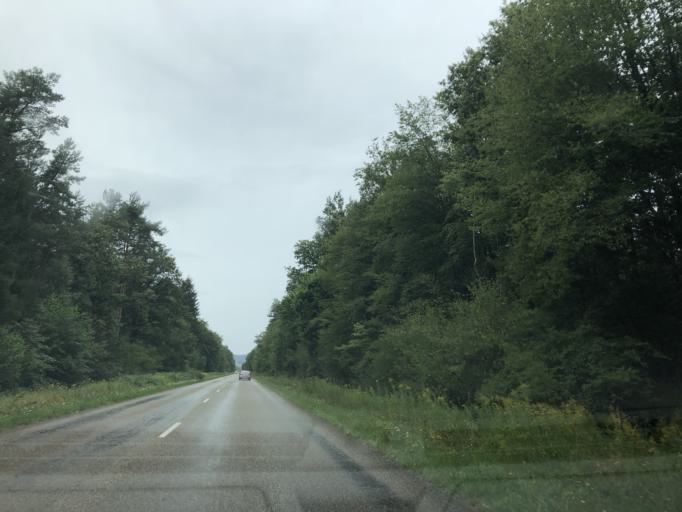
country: DE
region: Rheinland-Pfalz
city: Schweighofen
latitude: 49.0195
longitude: 8.0018
